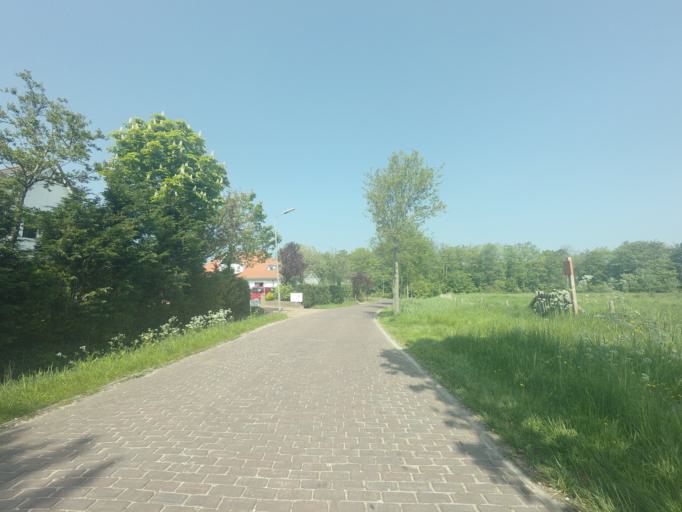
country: NL
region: Zeeland
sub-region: Gemeente Middelburg
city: Middelburg
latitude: 51.5677
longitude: 3.5424
